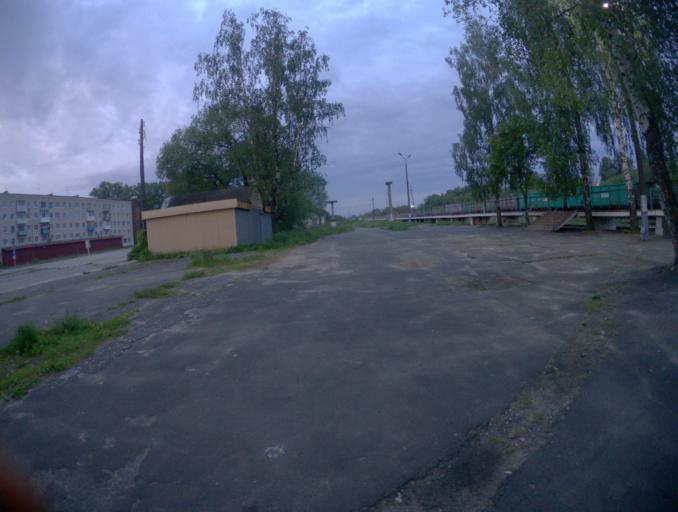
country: RU
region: Vladimir
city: Gus'-Khrustal'nyy
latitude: 55.6183
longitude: 40.6504
